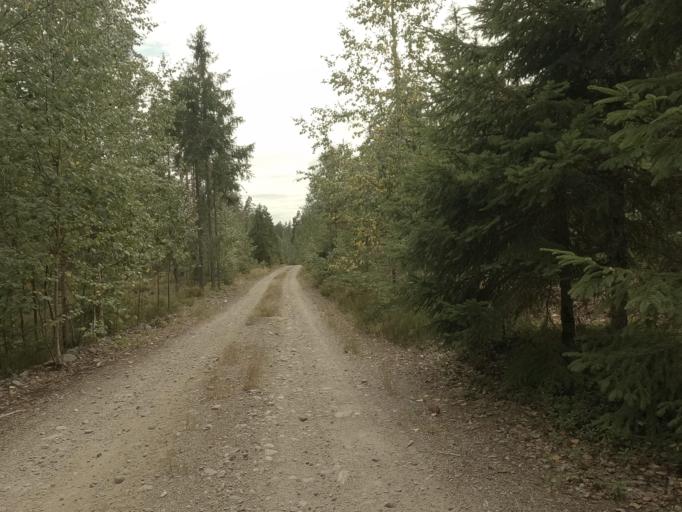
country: RU
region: Leningrad
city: Kamennogorsk
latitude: 61.0132
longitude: 29.2074
